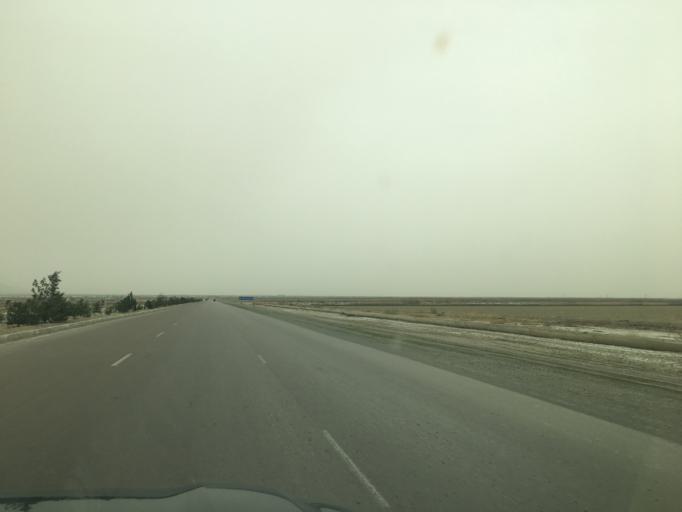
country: TM
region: Ahal
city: Baharly
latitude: 38.3720
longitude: 57.5153
